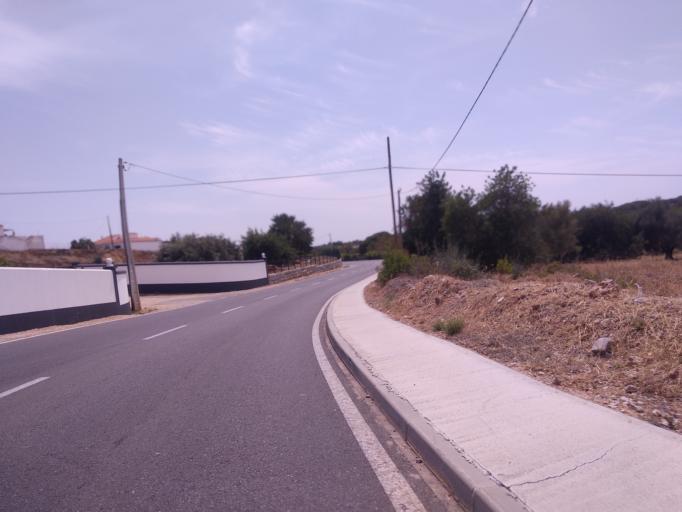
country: PT
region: Faro
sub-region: Faro
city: Santa Barbara de Nexe
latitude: 37.0846
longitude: -7.9938
